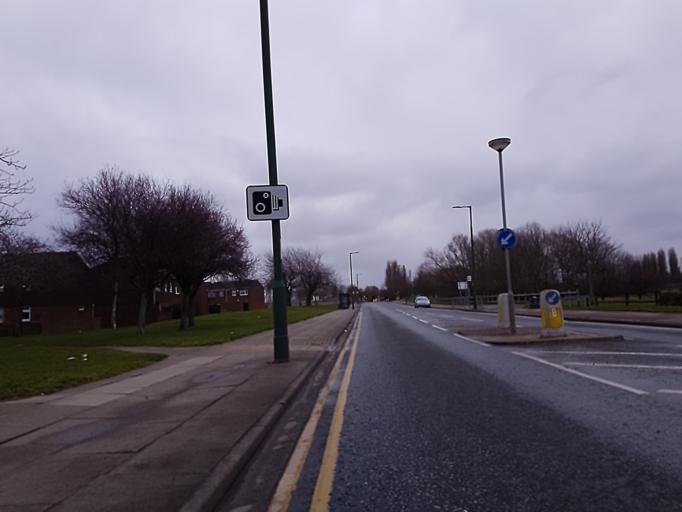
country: GB
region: England
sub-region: North East Lincolnshire
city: Great Coates
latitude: 53.5706
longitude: -0.1192
